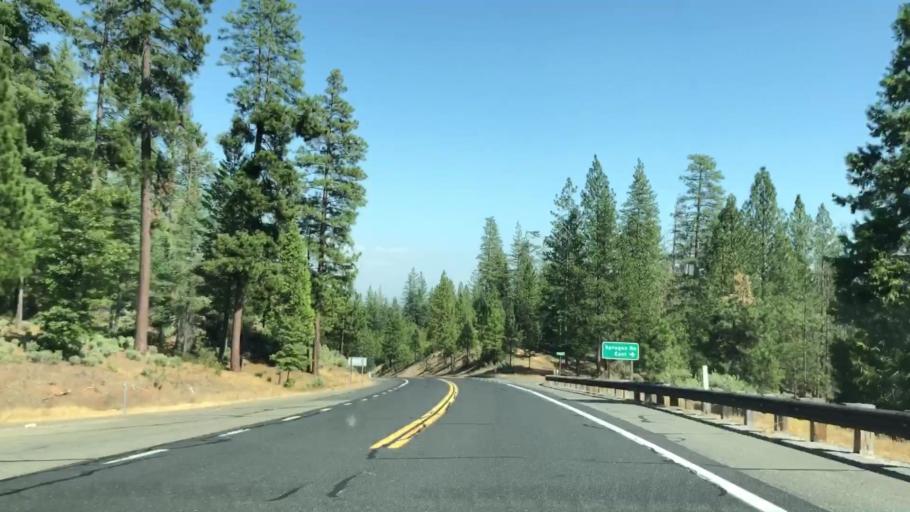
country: US
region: California
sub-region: Tuolumne County
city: Tuolumne City
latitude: 37.8207
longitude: -120.1572
